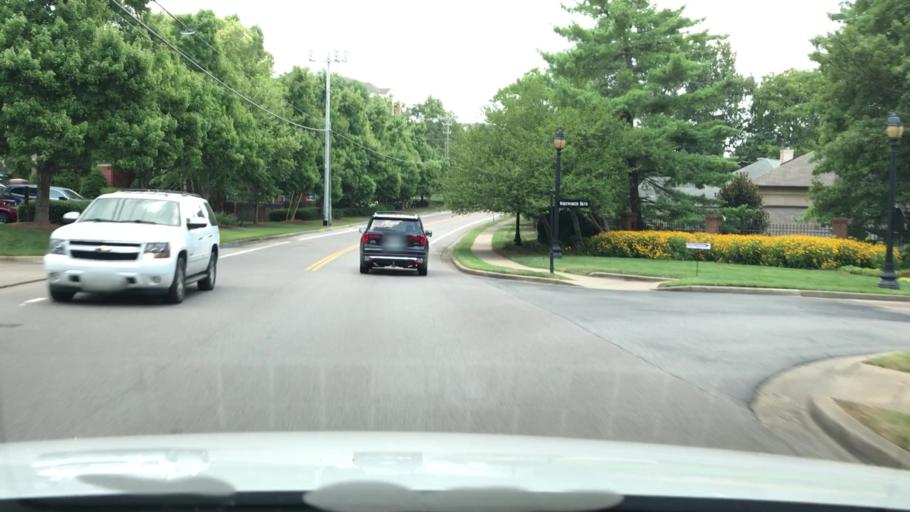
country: US
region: Tennessee
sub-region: Davidson County
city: Belle Meade
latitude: 36.1299
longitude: -86.8204
